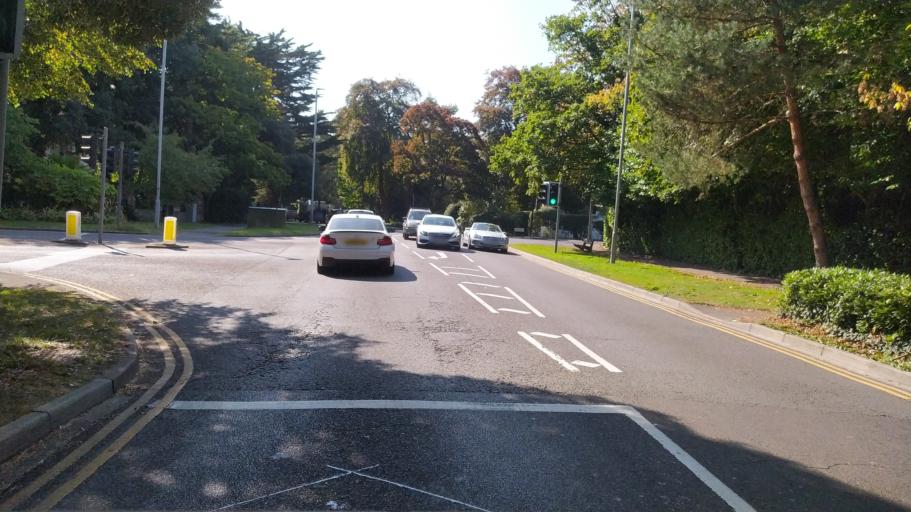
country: GB
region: England
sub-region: Bournemouth
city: Bournemouth
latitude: 50.7185
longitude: -1.9090
